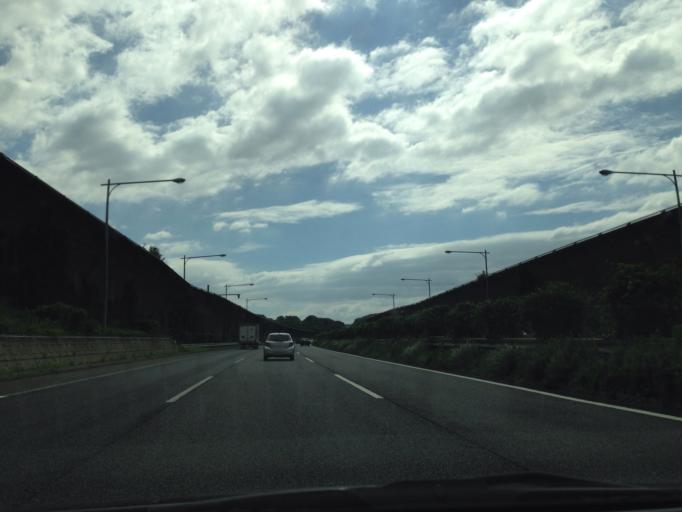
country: JP
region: Kanagawa
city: Hadano
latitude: 35.3622
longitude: 139.2543
